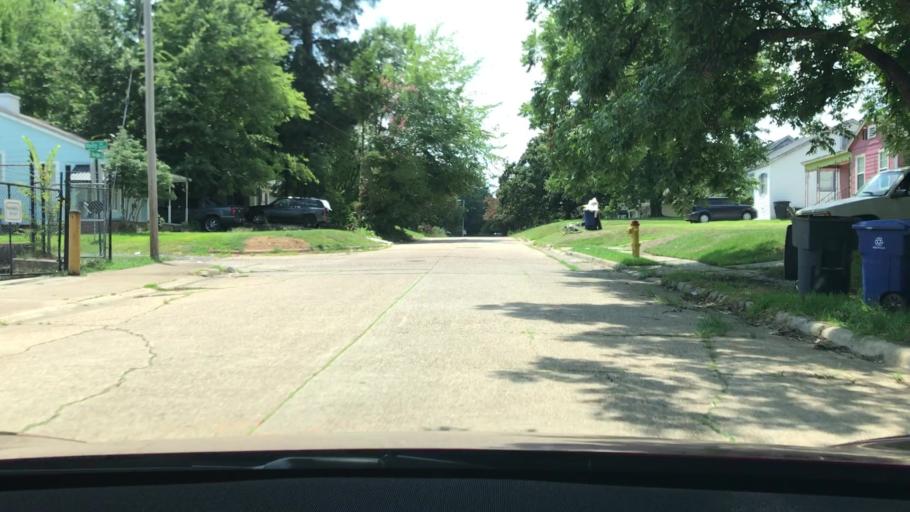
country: US
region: Louisiana
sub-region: Bossier Parish
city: Bossier City
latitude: 32.4964
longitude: -93.7267
